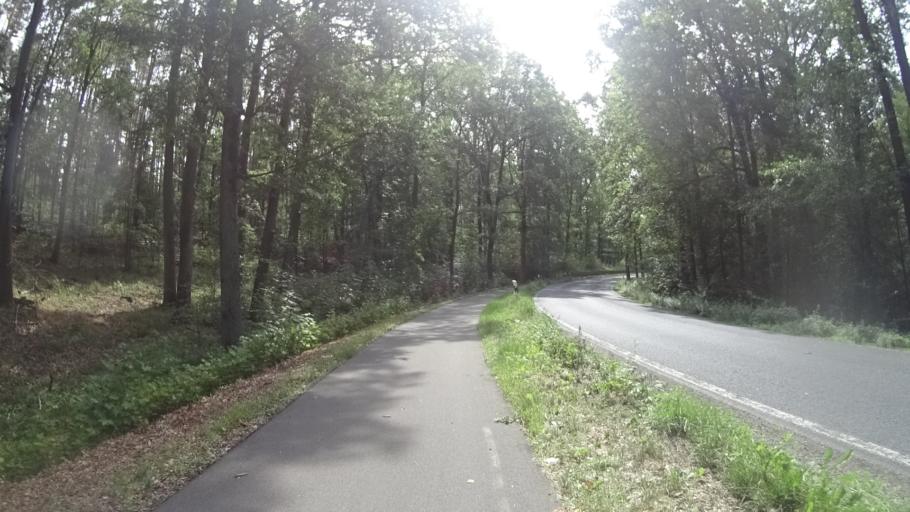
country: DE
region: Brandenburg
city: Borkwalde
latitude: 52.3067
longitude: 12.7637
